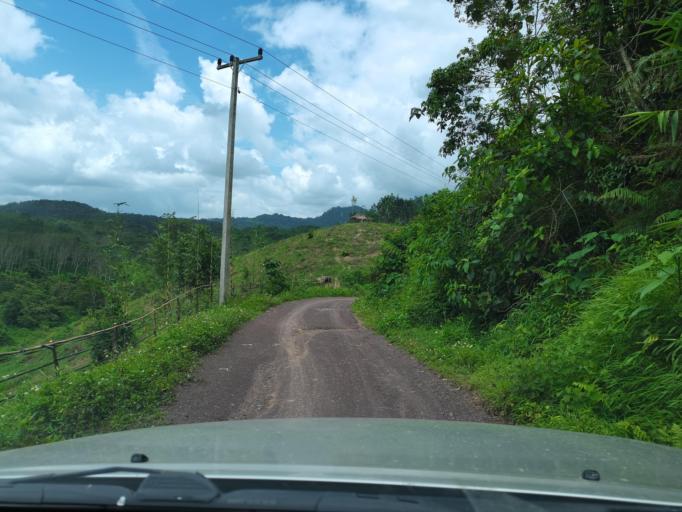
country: LA
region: Loungnamtha
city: Muang Long
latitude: 20.7024
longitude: 101.0149
